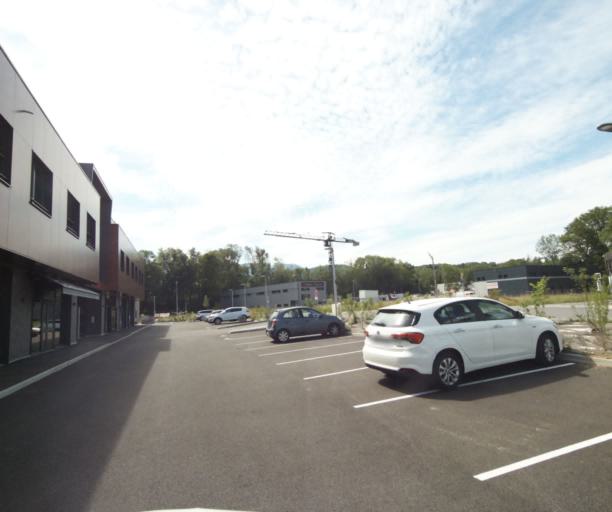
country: FR
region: Rhone-Alpes
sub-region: Departement de la Haute-Savoie
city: Anthy-sur-Leman
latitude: 46.3518
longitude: 6.4454
